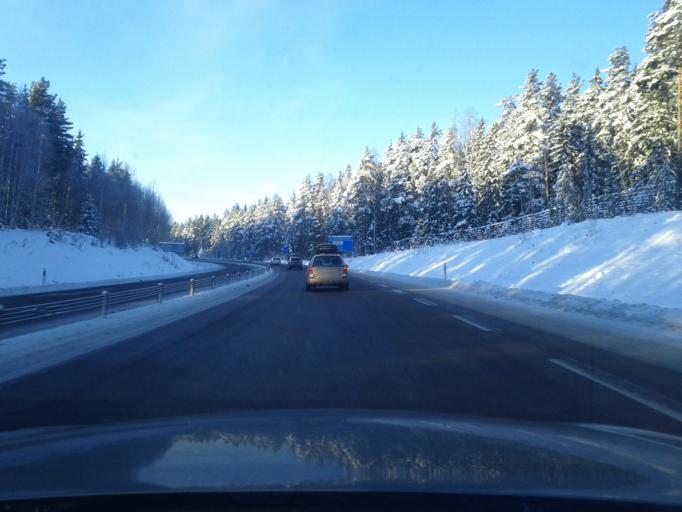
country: SE
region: Dalarna
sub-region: Faluns Kommun
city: Falun
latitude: 60.5971
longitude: 15.6938
